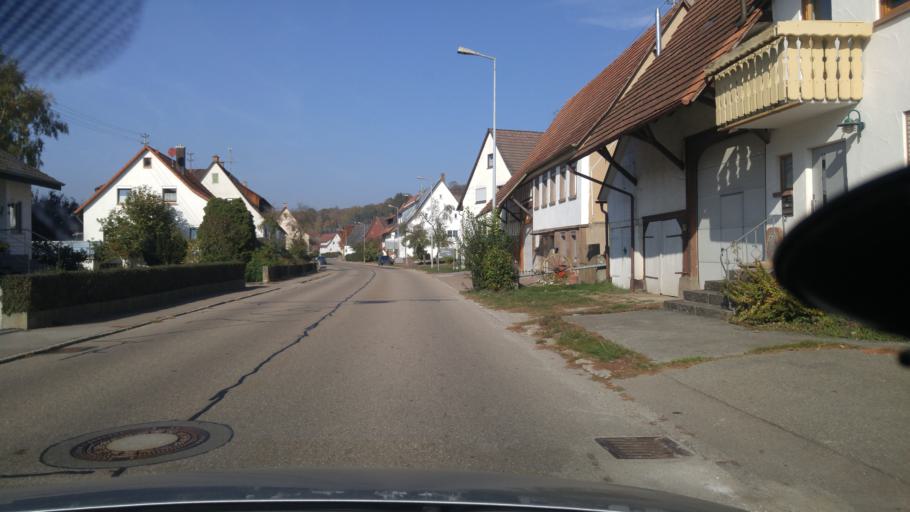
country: DE
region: Baden-Wuerttemberg
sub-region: Freiburg Region
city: Muhlheim am Bach
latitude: 48.3777
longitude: 8.7016
